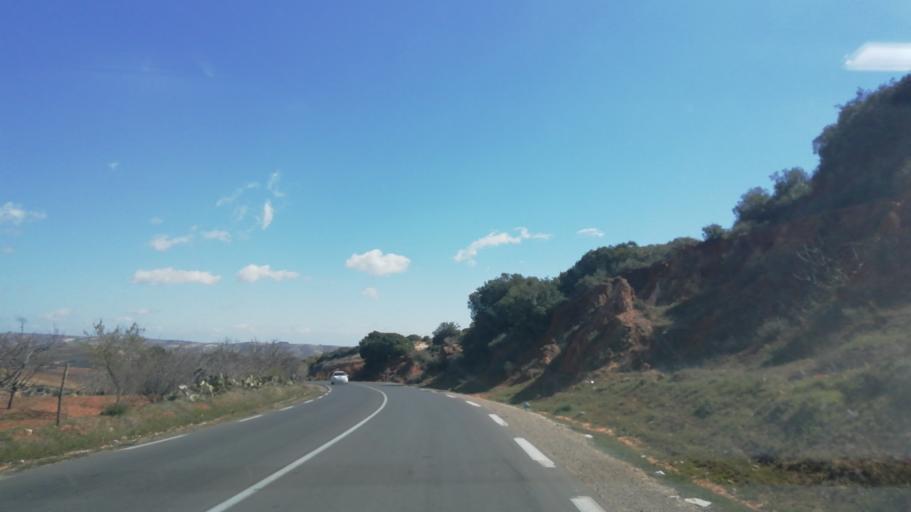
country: DZ
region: Mascara
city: Mascara
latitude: 35.4567
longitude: 0.1514
